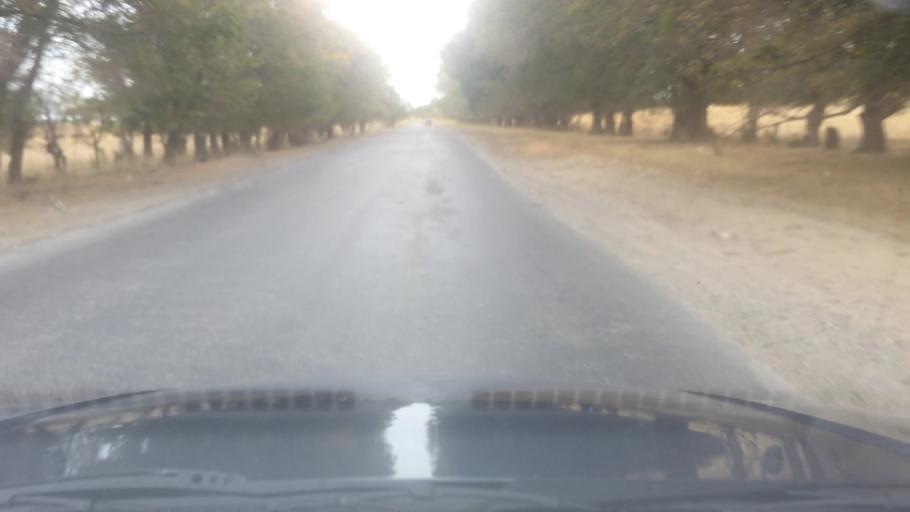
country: KG
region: Ysyk-Koel
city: Balykchy
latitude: 42.3087
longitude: 76.4633
